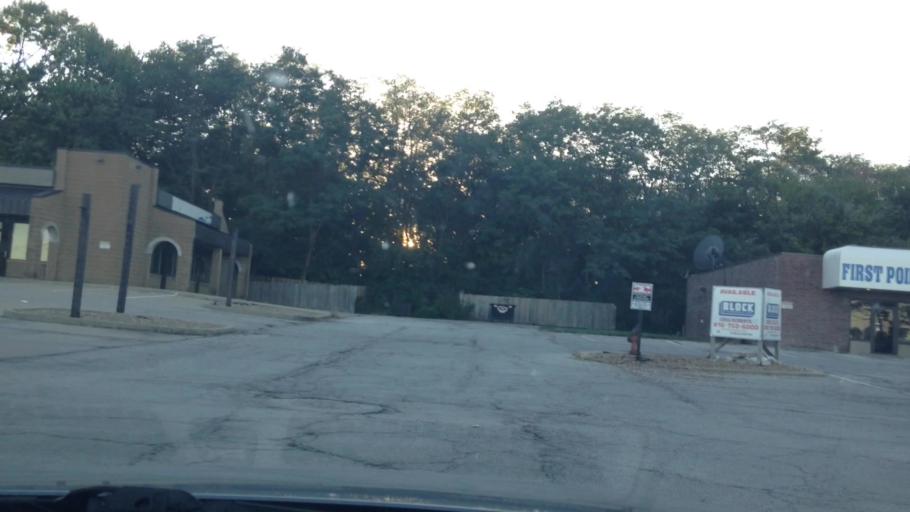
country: US
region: Missouri
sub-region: Platte County
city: Weatherby Lake
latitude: 39.2424
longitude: -94.6595
